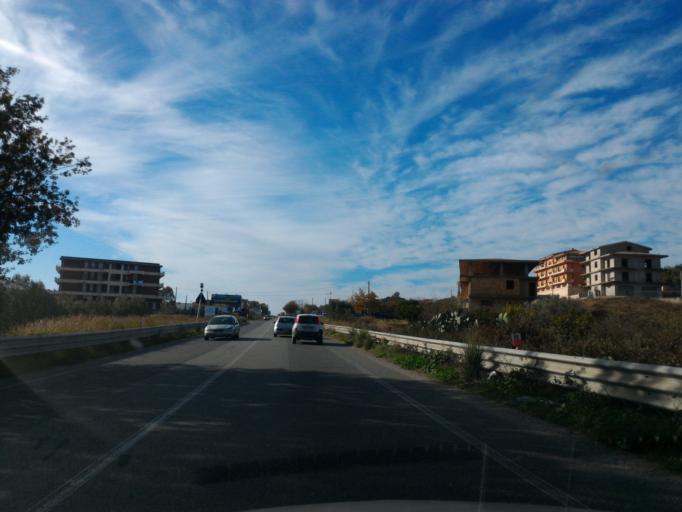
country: IT
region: Calabria
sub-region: Provincia di Catanzaro
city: Sellia Marina
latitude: 38.8924
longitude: 16.7222
